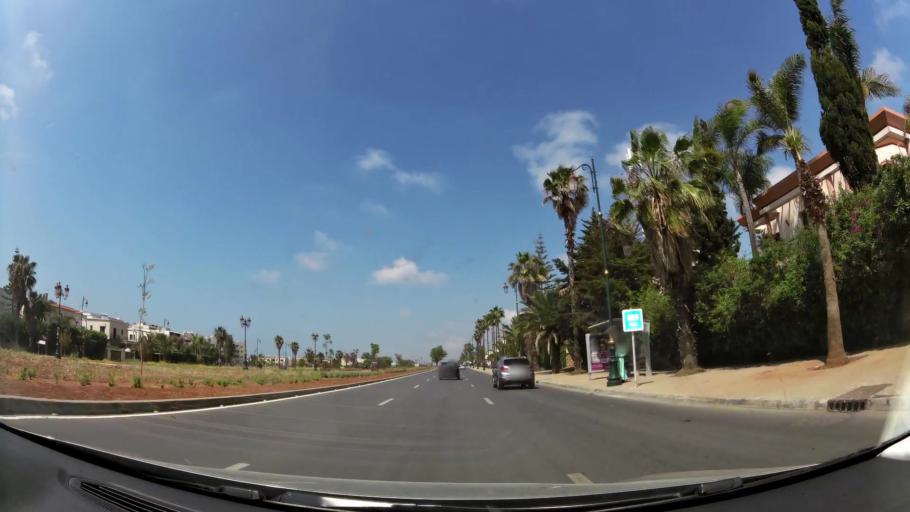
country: MA
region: Rabat-Sale-Zemmour-Zaer
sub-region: Skhirate-Temara
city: Temara
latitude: 33.9581
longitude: -6.8772
